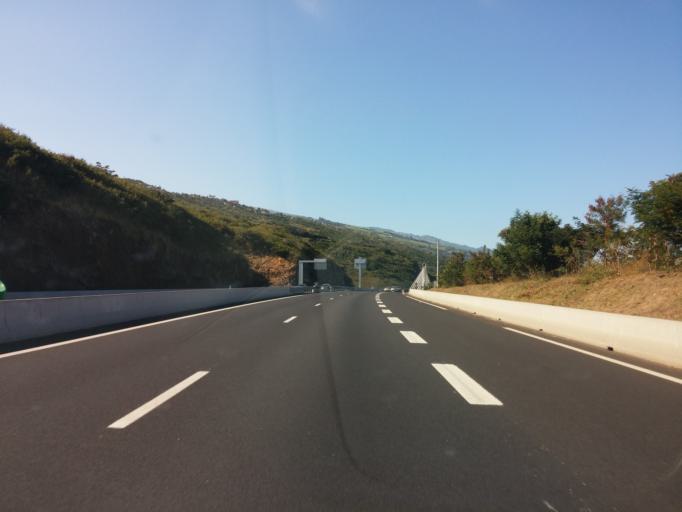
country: RE
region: Reunion
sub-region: Reunion
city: Trois-Bassins
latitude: -21.1029
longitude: 55.2693
